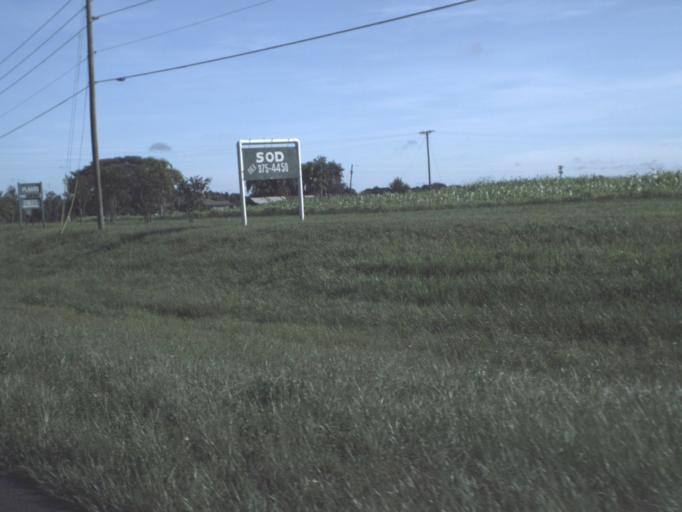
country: US
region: Florida
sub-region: Hardee County
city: Bowling Green
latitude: 27.6121
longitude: -81.8261
